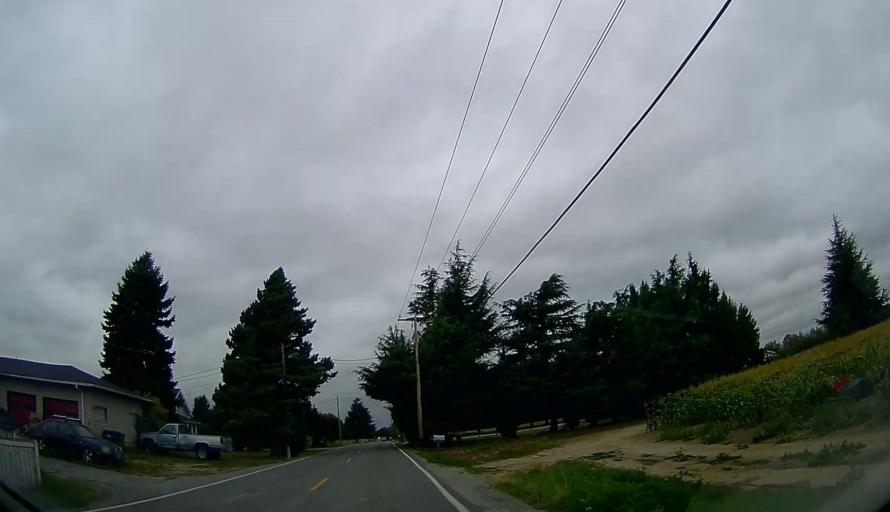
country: US
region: Washington
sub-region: Skagit County
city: Burlington
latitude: 48.4540
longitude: -122.3493
